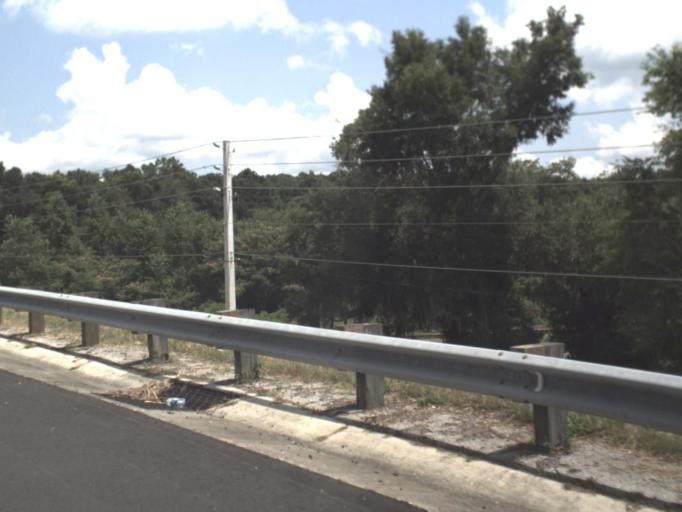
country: US
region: Florida
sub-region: Alachua County
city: Alachua
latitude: 29.7868
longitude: -82.4769
